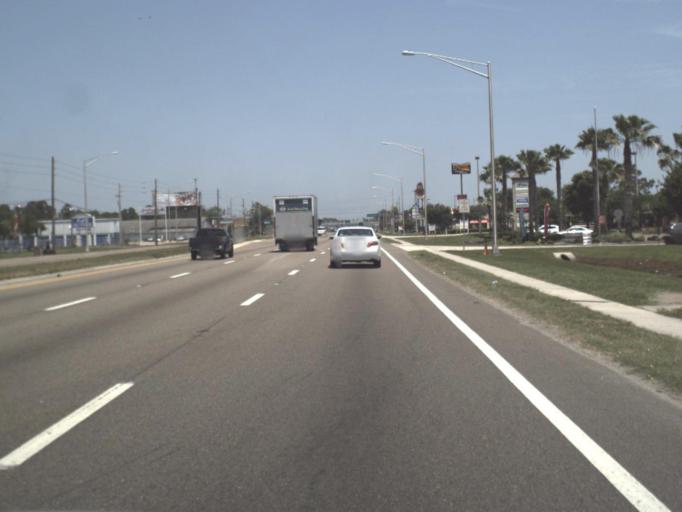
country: US
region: Florida
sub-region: Duval County
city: Jacksonville
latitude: 30.2867
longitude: -81.5333
